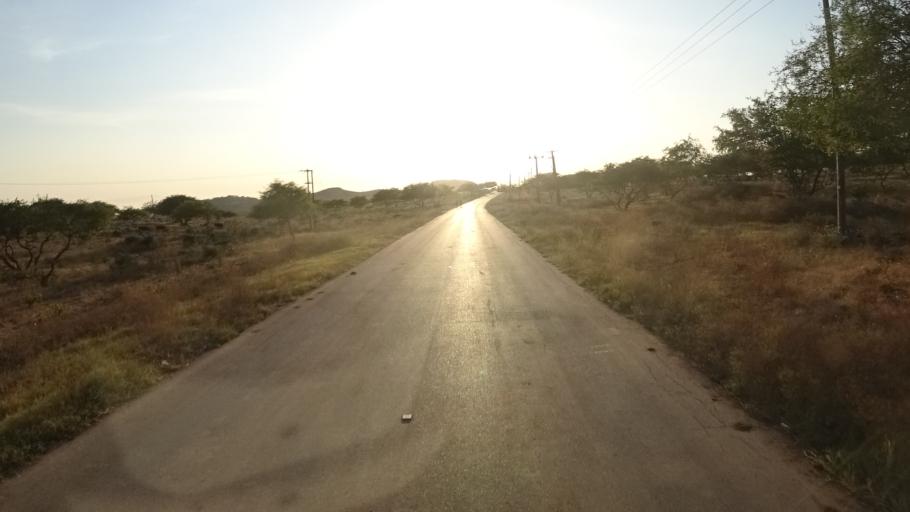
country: OM
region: Zufar
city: Salalah
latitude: 17.1484
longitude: 54.5946
